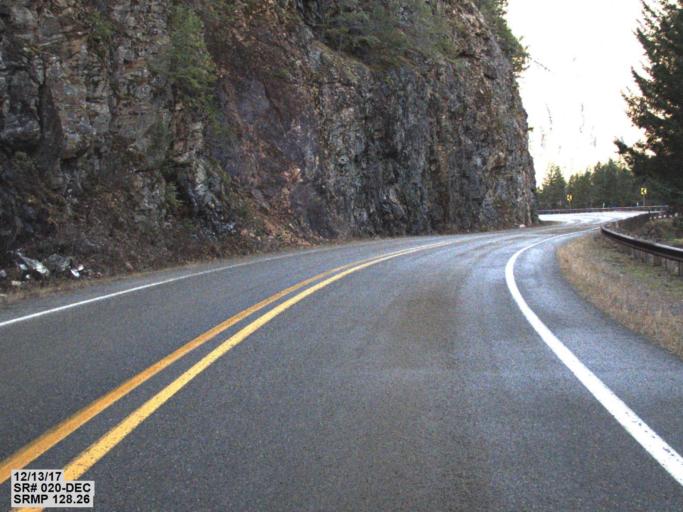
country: US
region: Washington
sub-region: Snohomish County
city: Darrington
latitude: 48.7100
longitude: -121.1205
